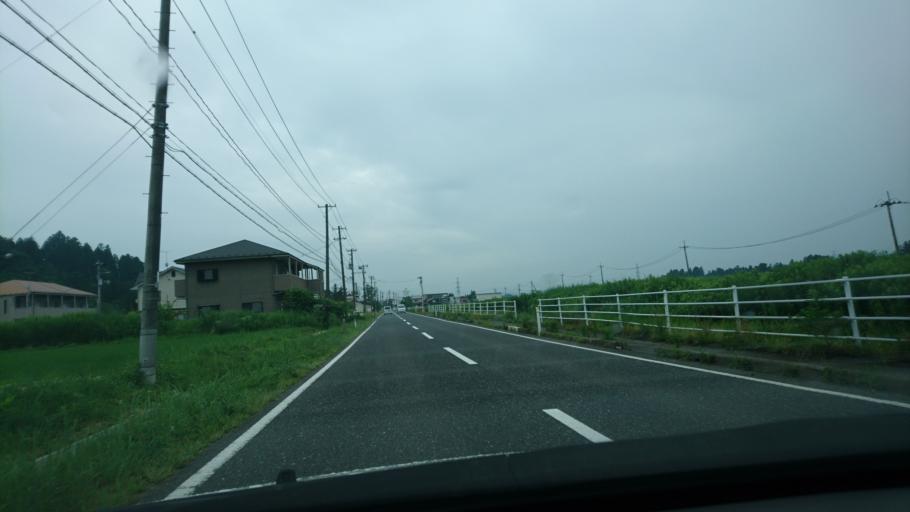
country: JP
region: Miyagi
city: Furukawa
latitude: 38.7299
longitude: 140.9853
